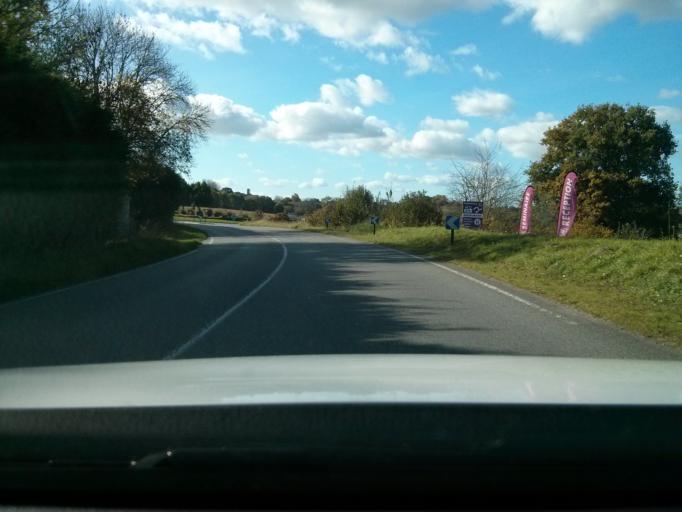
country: FR
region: Brittany
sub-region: Departement des Cotes-d'Armor
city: Ploubalay
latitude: 48.5759
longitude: -2.1746
